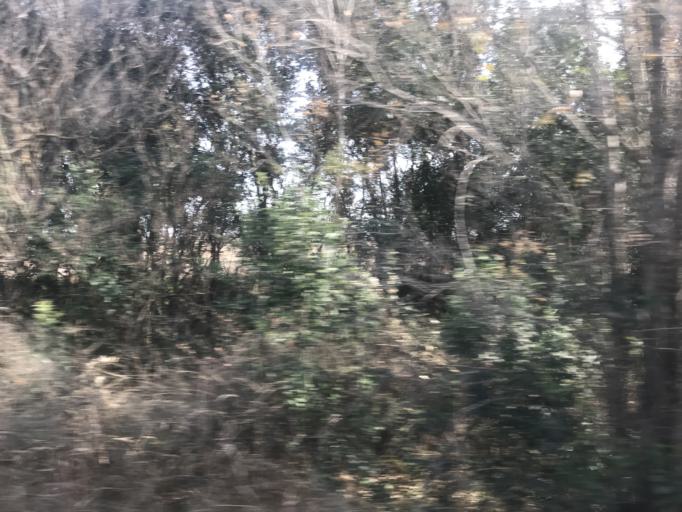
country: AR
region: Cordoba
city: Laguna Larga
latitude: -31.7657
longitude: -63.8129
